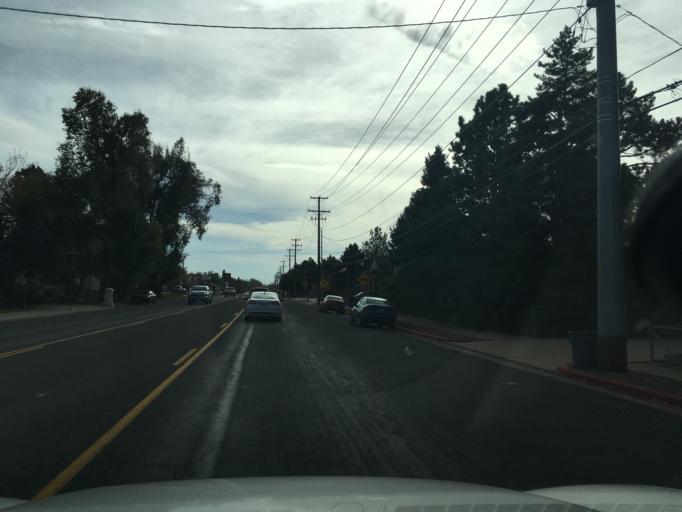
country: US
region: Utah
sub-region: Davis County
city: Layton
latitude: 41.0641
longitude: -111.9576
